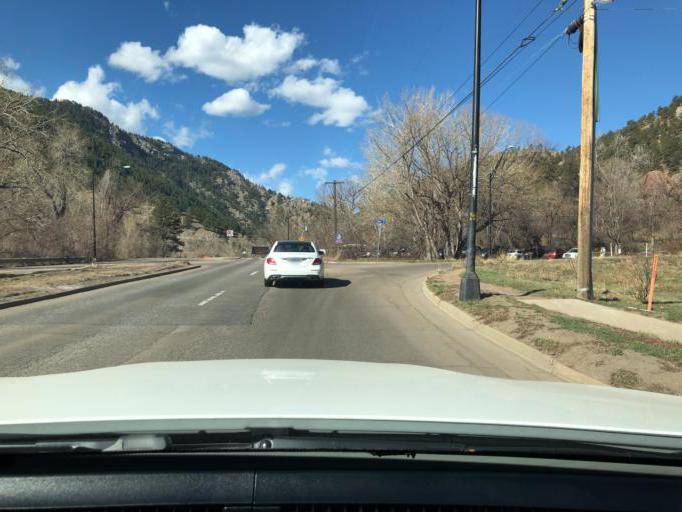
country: US
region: Colorado
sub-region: Boulder County
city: Boulder
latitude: 40.0140
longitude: -105.2942
